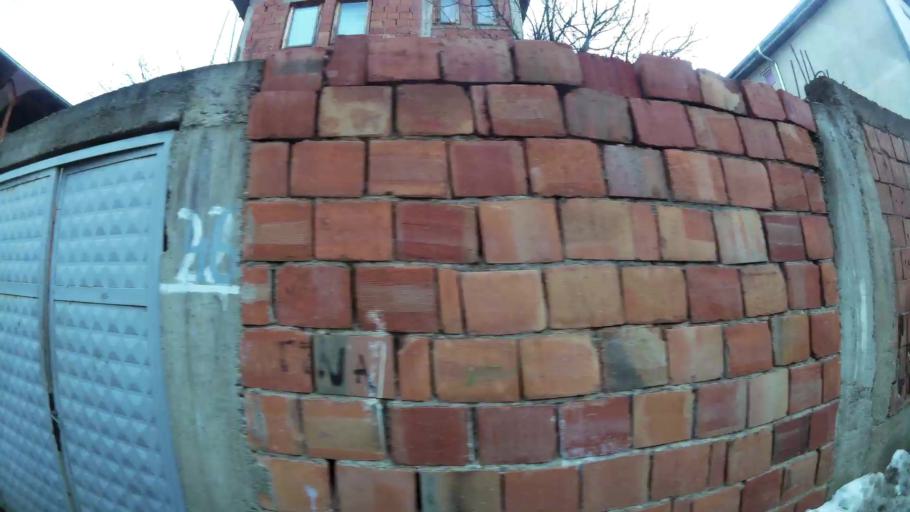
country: XK
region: Pristina
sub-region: Komuna e Prishtines
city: Pristina
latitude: 42.6712
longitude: 21.1751
